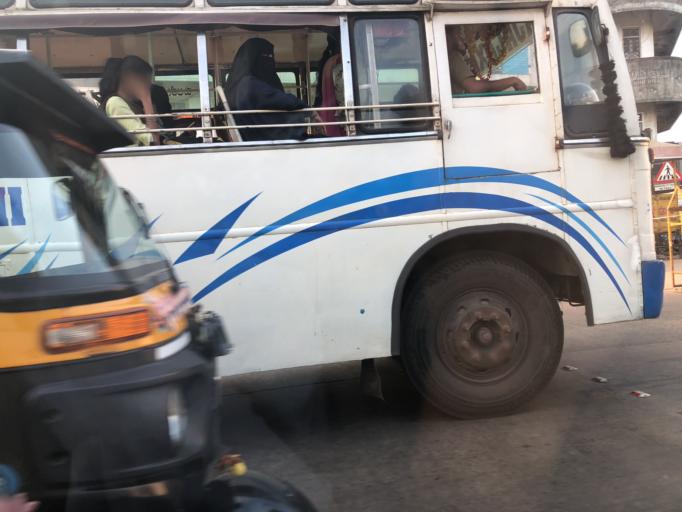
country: IN
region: Karnataka
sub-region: Dakshina Kannada
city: Mangalore
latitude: 12.8665
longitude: 74.8408
